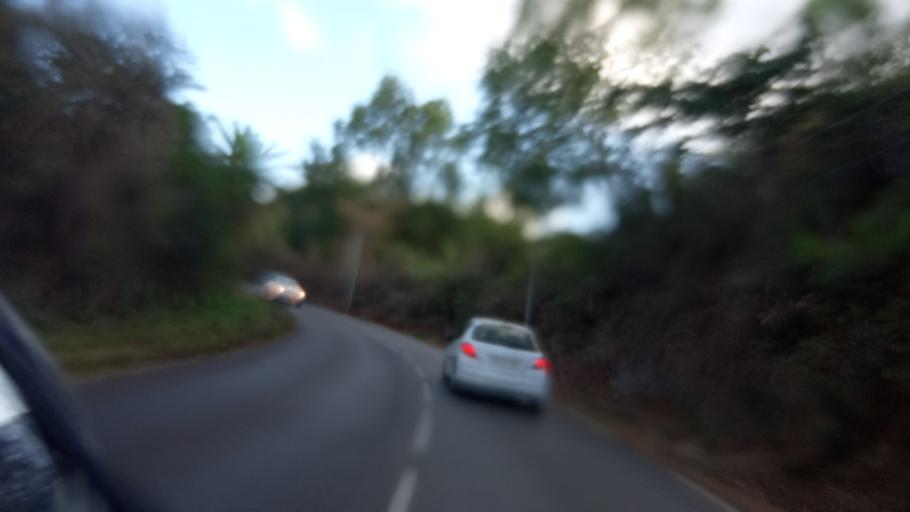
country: YT
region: Dembeni
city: Dembeni
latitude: -12.8485
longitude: 45.1908
